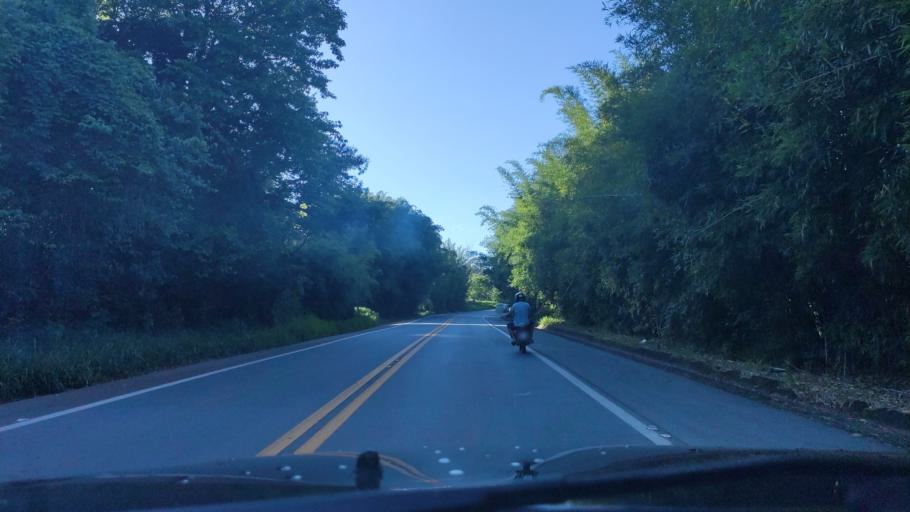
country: BR
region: Sao Paulo
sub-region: Socorro
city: Socorro
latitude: -22.5617
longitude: -46.5500
